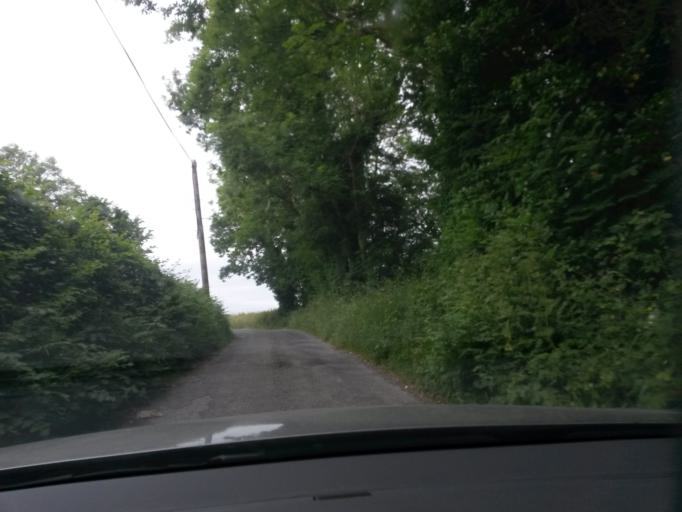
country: IE
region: Munster
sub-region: An Clar
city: Ennis
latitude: 52.9155
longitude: -9.0498
